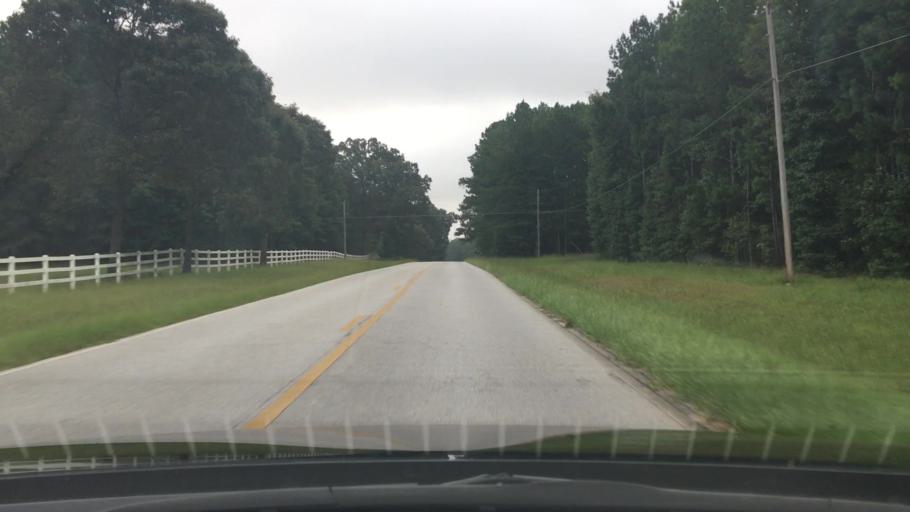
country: US
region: Georgia
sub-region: Spalding County
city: Experiment
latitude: 33.2811
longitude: -84.4067
